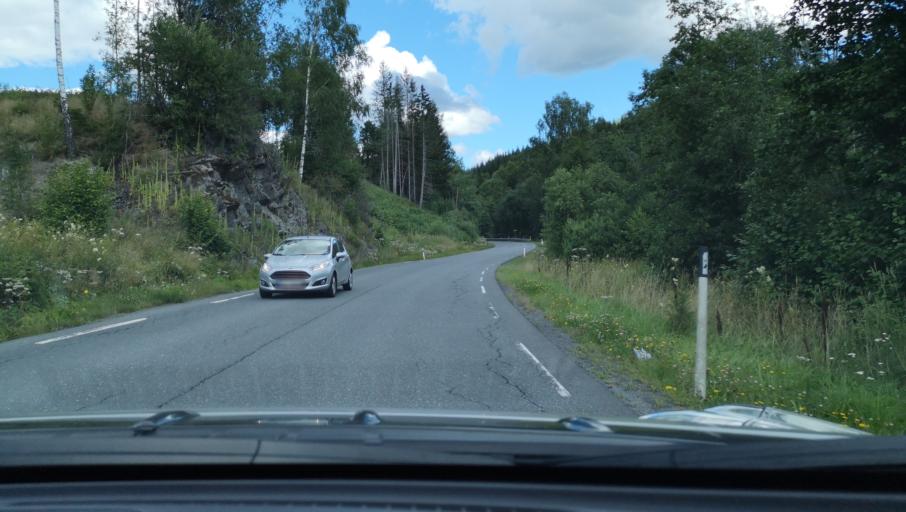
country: NO
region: Ostfold
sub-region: Hobol
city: Tomter
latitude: 59.6461
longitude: 10.9861
